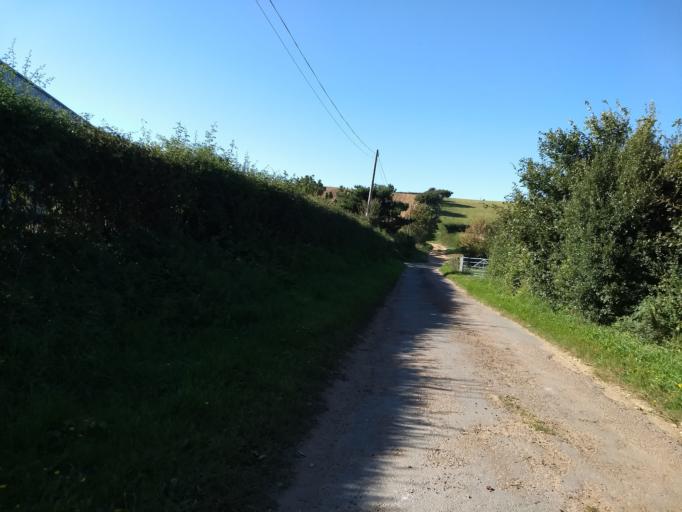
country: GB
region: England
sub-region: Isle of Wight
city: Chale
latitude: 50.6403
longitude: -1.2996
